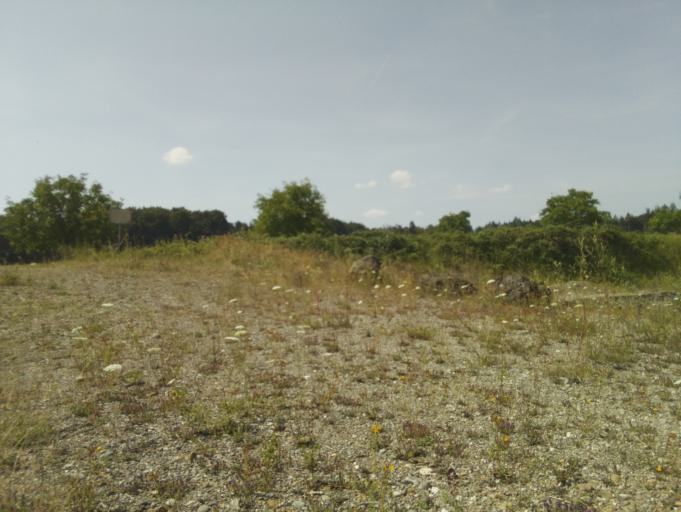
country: CH
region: Zurich
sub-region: Bezirk Andelfingen
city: Kleinandelfingen
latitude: 47.6110
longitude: 8.7108
